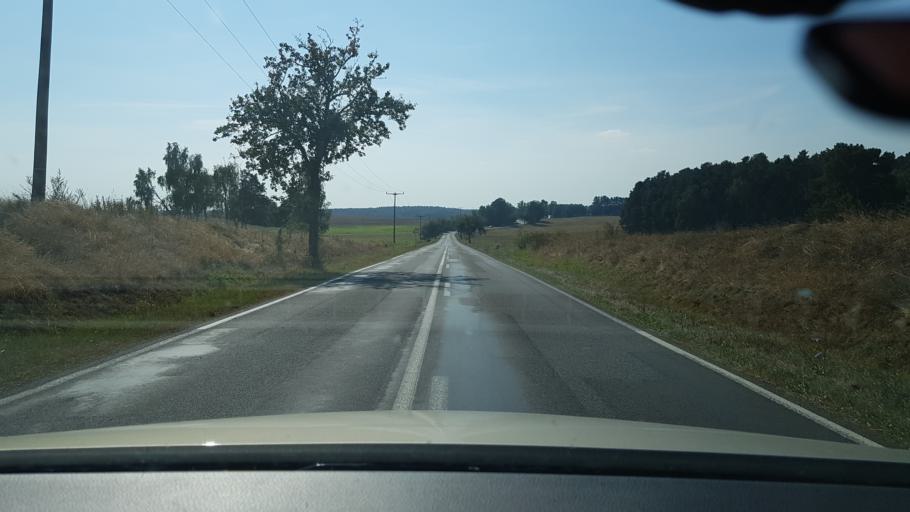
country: DE
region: Brandenburg
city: Lawitz
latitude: 52.1187
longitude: 14.5897
